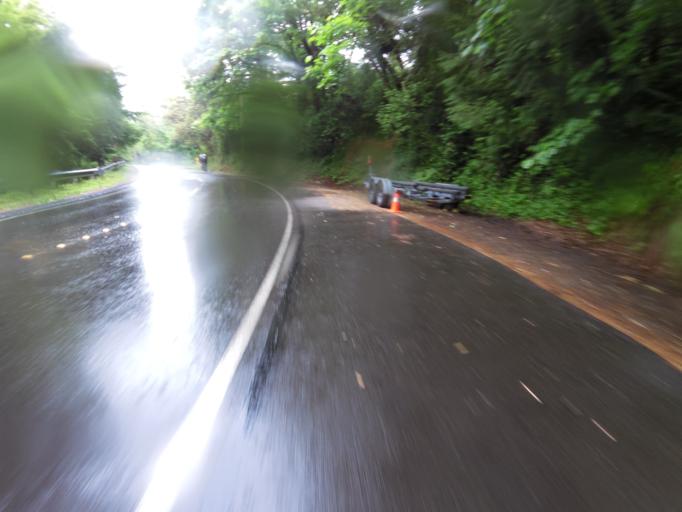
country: US
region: Washington
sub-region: King County
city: Bryn Mawr-Skyway
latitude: 47.5337
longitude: -122.2390
